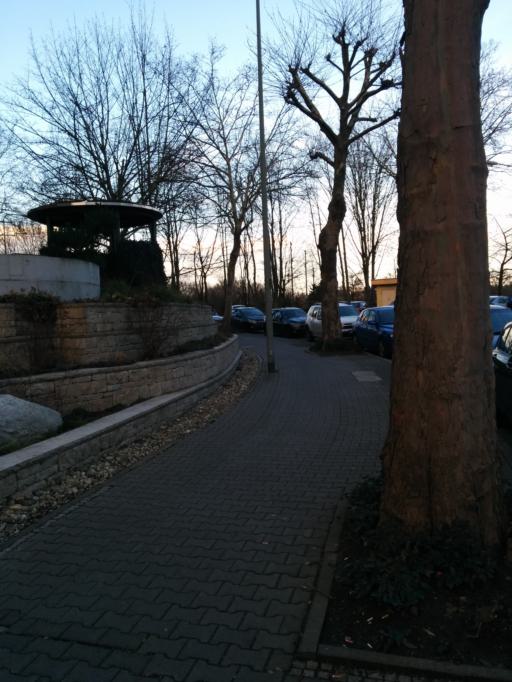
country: DE
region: Hesse
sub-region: Regierungsbezirk Darmstadt
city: Eschborn
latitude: 50.1354
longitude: 8.5730
